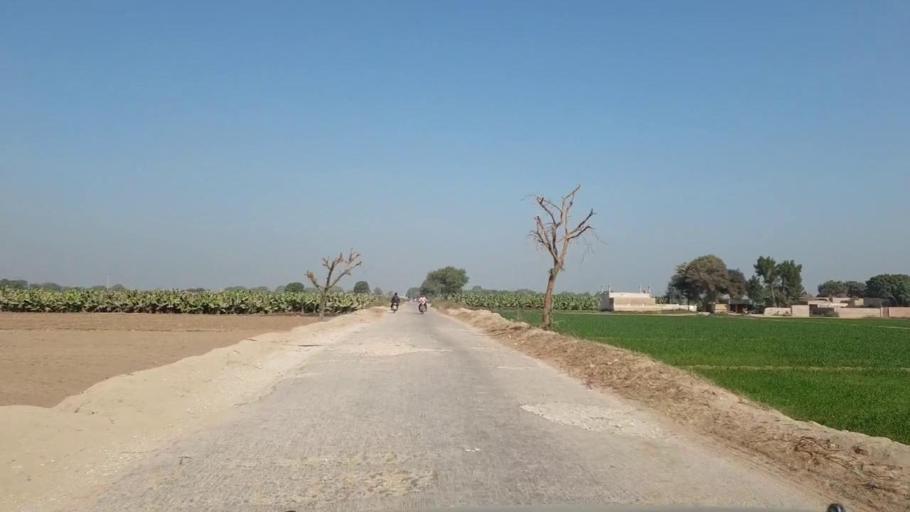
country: PK
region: Sindh
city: Matiari
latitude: 25.5923
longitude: 68.6010
